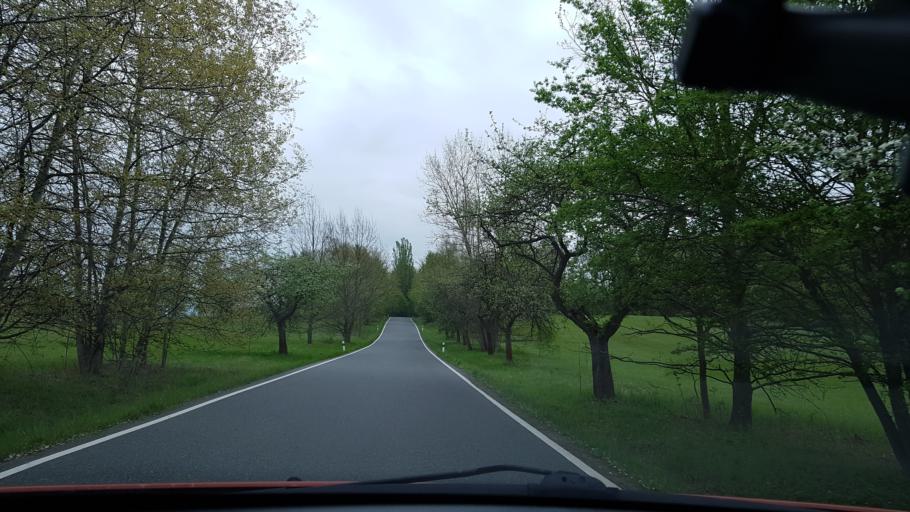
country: CZ
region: Olomoucky
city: Vidnava
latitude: 50.3648
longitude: 17.1991
